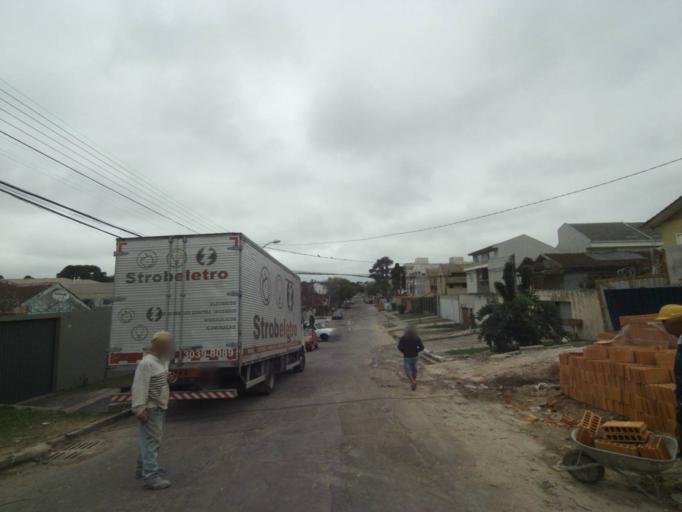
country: BR
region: Parana
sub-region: Curitiba
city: Curitiba
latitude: -25.4673
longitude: -49.2745
